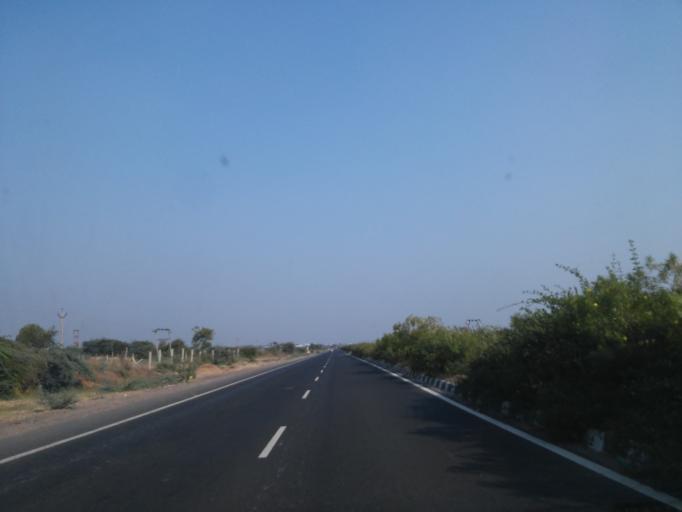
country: IN
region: Gujarat
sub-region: Surendranagar
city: Halvad
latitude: 23.0052
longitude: 71.1209
